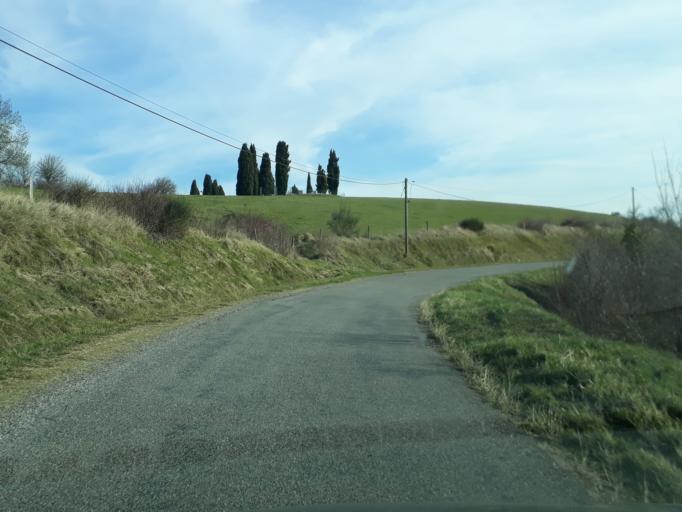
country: FR
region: Midi-Pyrenees
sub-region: Departement de la Haute-Garonne
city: Montesquieu-Volvestre
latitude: 43.1825
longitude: 1.2996
